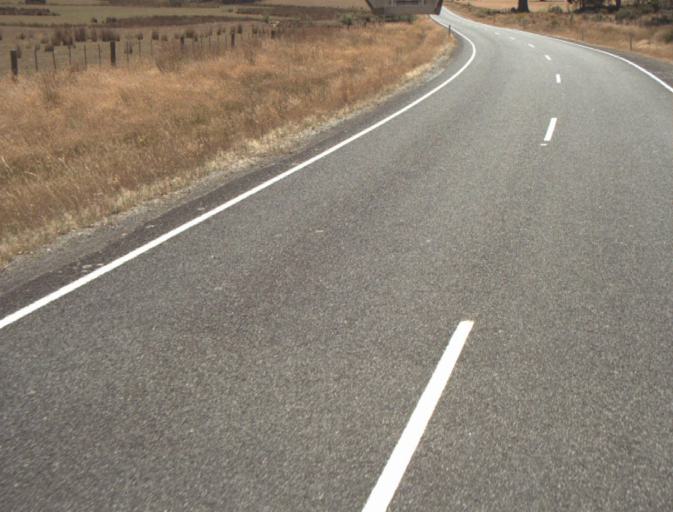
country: AU
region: Tasmania
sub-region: Dorset
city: Scottsdale
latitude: -41.2968
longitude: 147.3849
